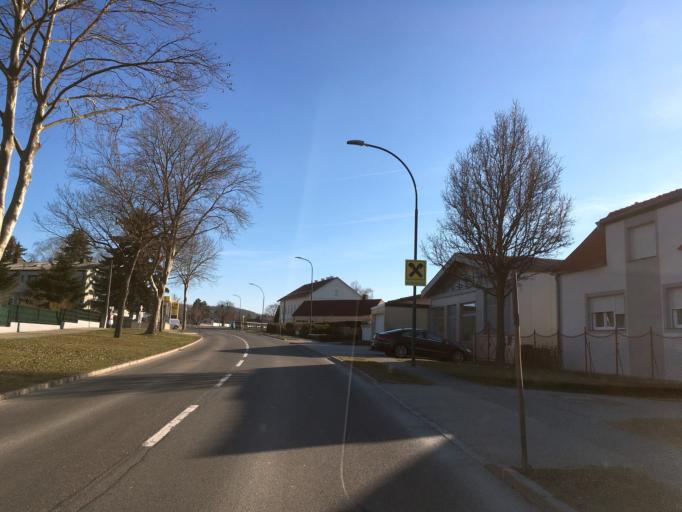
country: AT
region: Burgenland
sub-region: Eisenstadt-Umgebung
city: Hornstein
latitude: 47.8853
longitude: 16.4393
